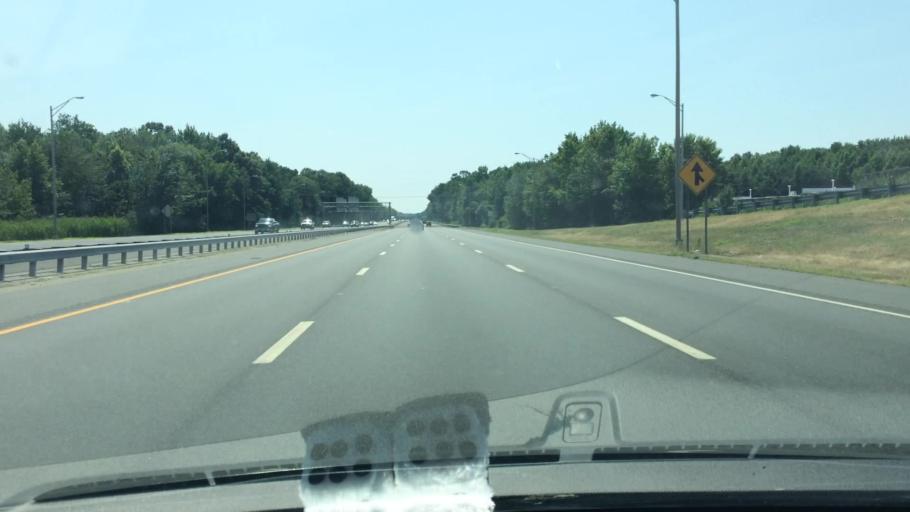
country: US
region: New Jersey
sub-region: Gloucester County
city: Paulsboro
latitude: 39.8152
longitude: -75.2587
